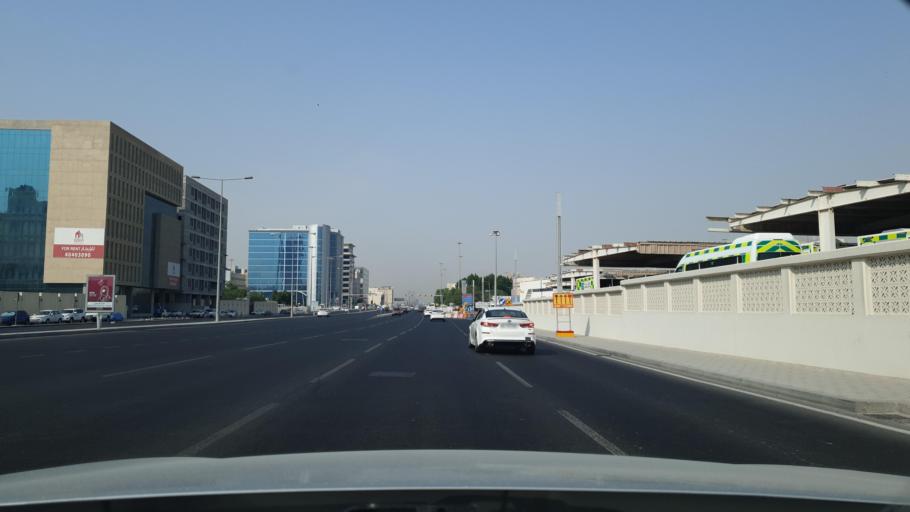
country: QA
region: Baladiyat ad Dawhah
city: Doha
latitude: 25.2902
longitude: 51.5105
